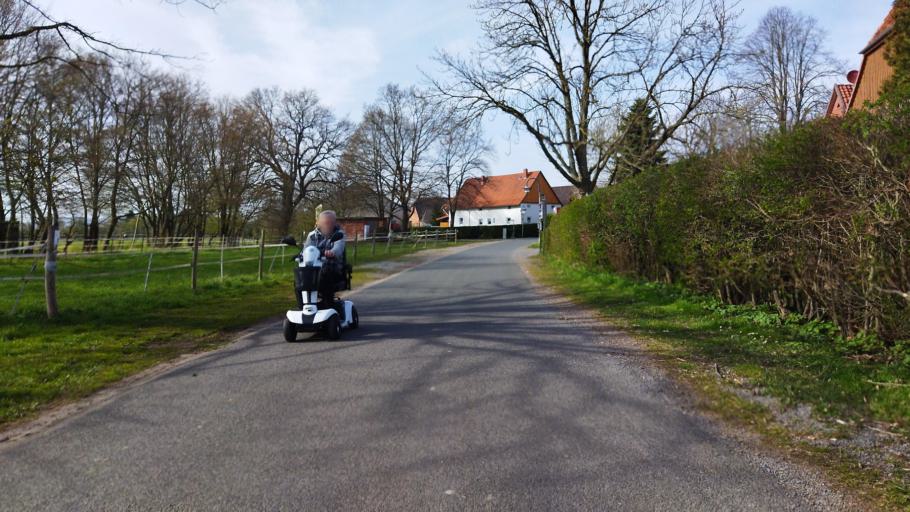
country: DE
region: Lower Saxony
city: Hessisch Oldendorf
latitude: 52.1699
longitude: 9.1937
